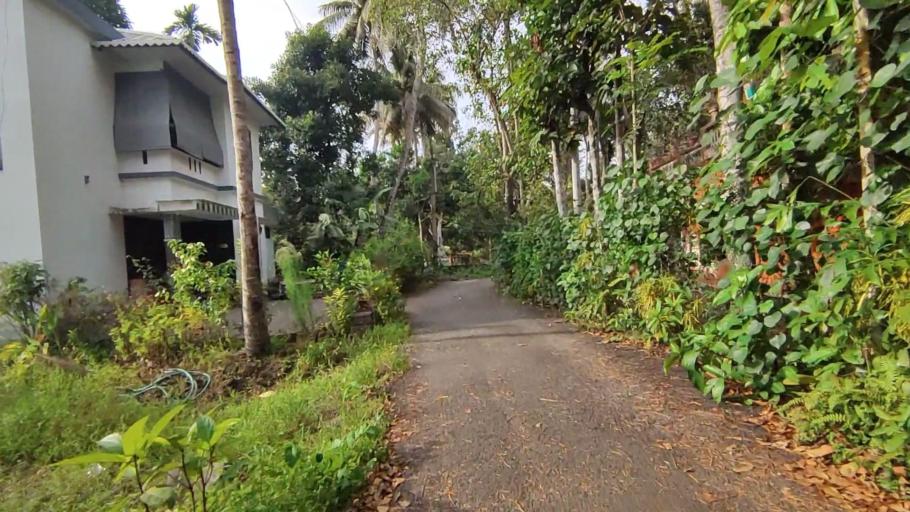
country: IN
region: Kerala
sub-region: Kottayam
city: Kottayam
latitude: 9.5718
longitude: 76.4912
